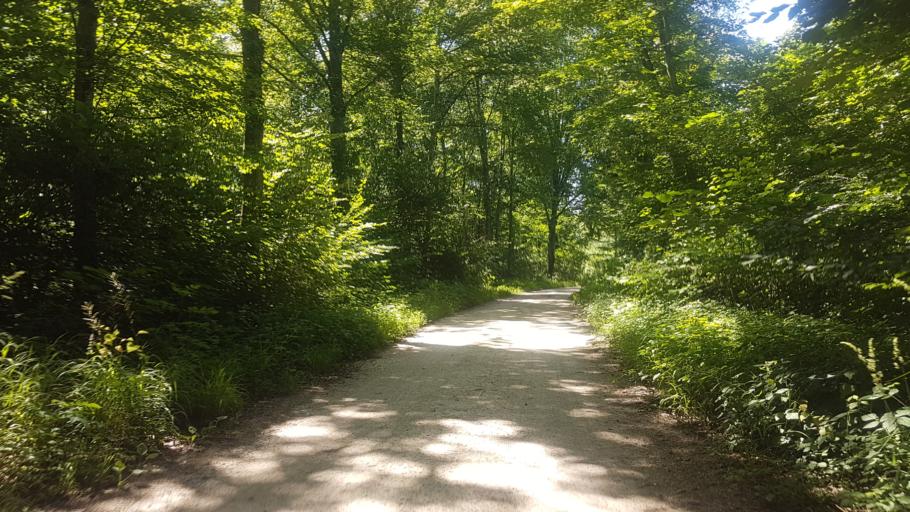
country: DE
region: Bavaria
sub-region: Upper Bavaria
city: Weichering
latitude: 48.7284
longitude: 11.3139
